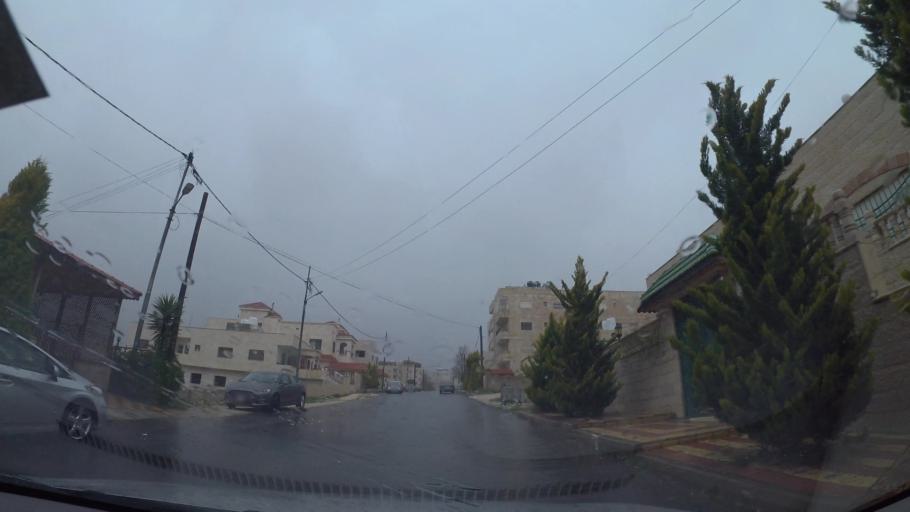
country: JO
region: Amman
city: Al Jubayhah
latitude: 32.0435
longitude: 35.8936
